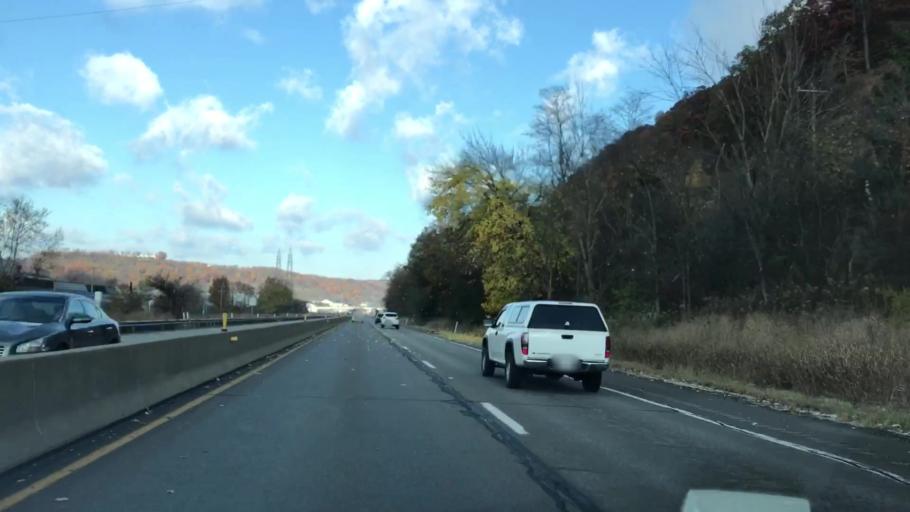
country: US
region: Pennsylvania
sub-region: Allegheny County
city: Leetsdale
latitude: 40.5720
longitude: -80.2175
